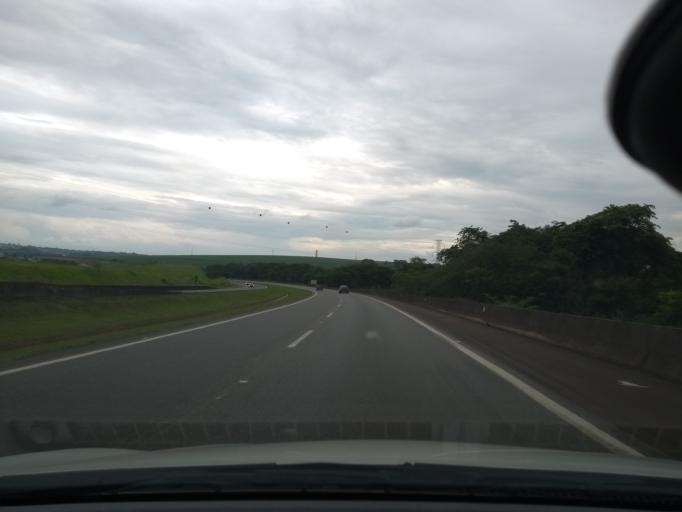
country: BR
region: Sao Paulo
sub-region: Cordeiropolis
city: Cordeiropolis
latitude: -22.5441
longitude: -47.4615
